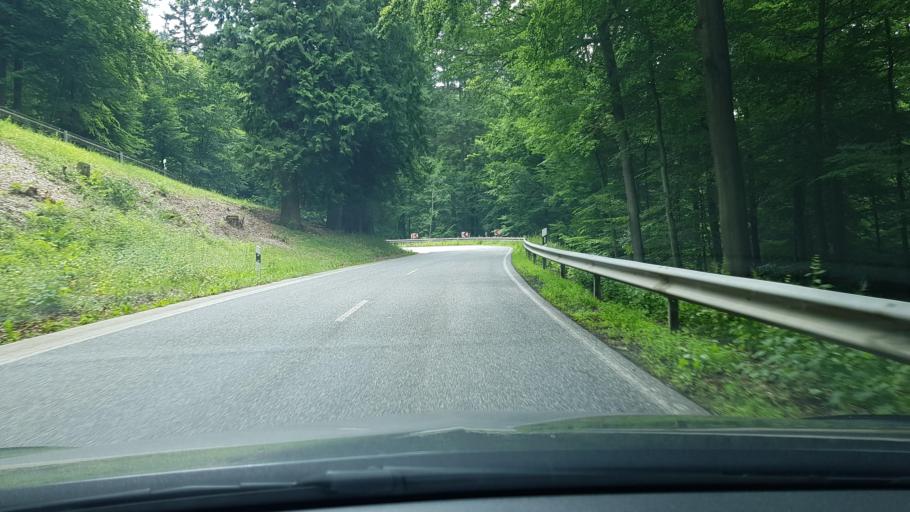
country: DE
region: Rheinland-Pfalz
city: Kaltenborn
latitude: 50.3873
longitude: 6.9957
